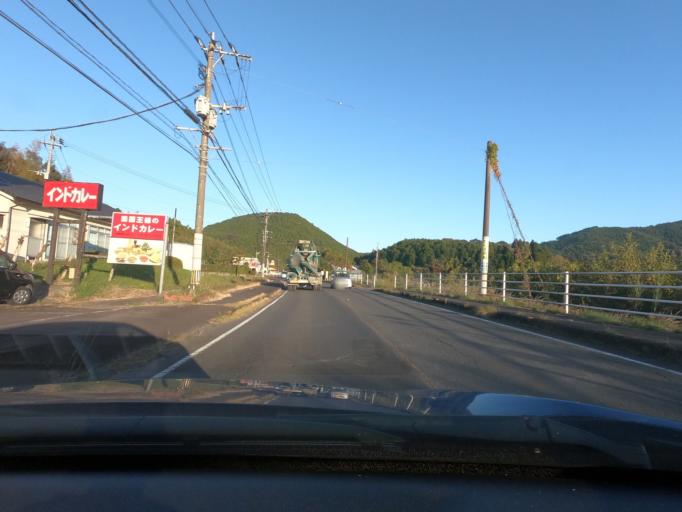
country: JP
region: Kagoshima
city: Satsumasendai
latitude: 31.8053
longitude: 130.3498
